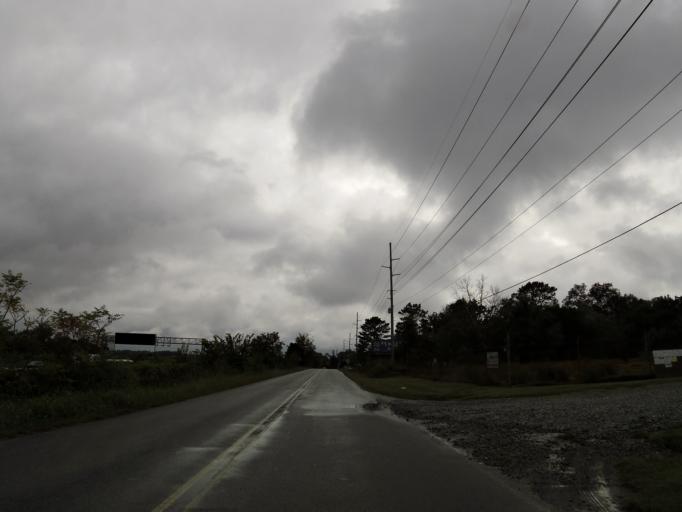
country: US
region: Tennessee
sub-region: Bradley County
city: Cleveland
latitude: 35.1801
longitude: -84.9132
